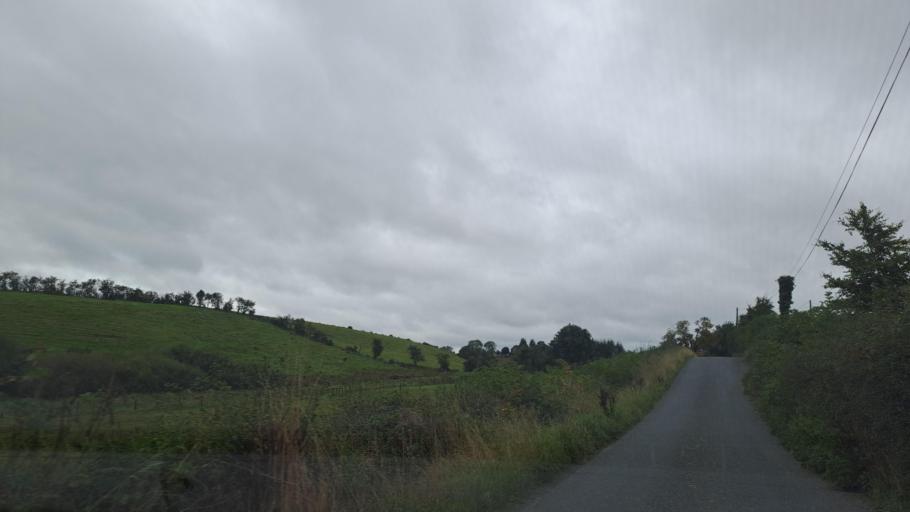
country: IE
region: Ulster
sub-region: An Cabhan
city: Kingscourt
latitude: 54.0001
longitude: -6.8466
